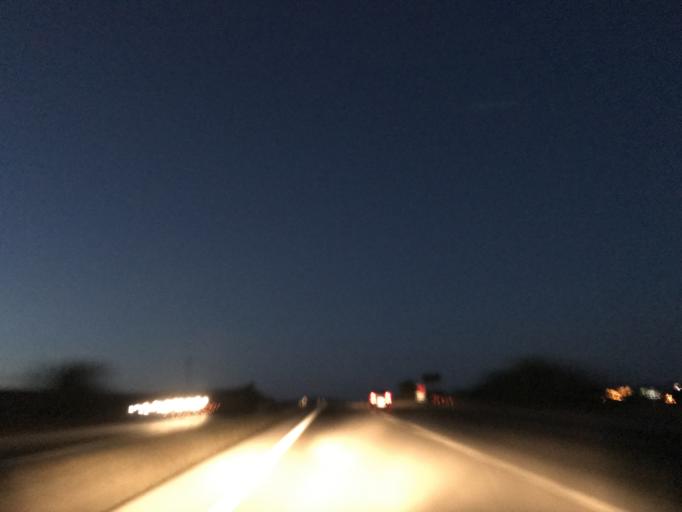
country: TR
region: Yozgat
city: Yerkoy
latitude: 39.6754
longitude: 34.5759
